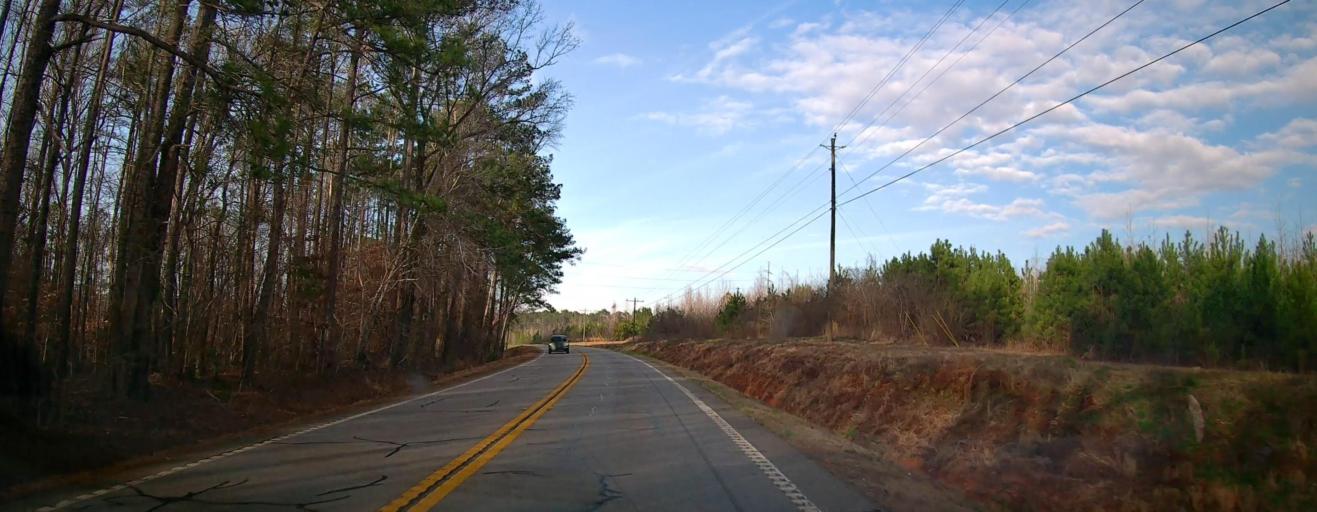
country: US
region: Georgia
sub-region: Harris County
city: Hamilton
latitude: 32.7371
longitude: -84.8707
